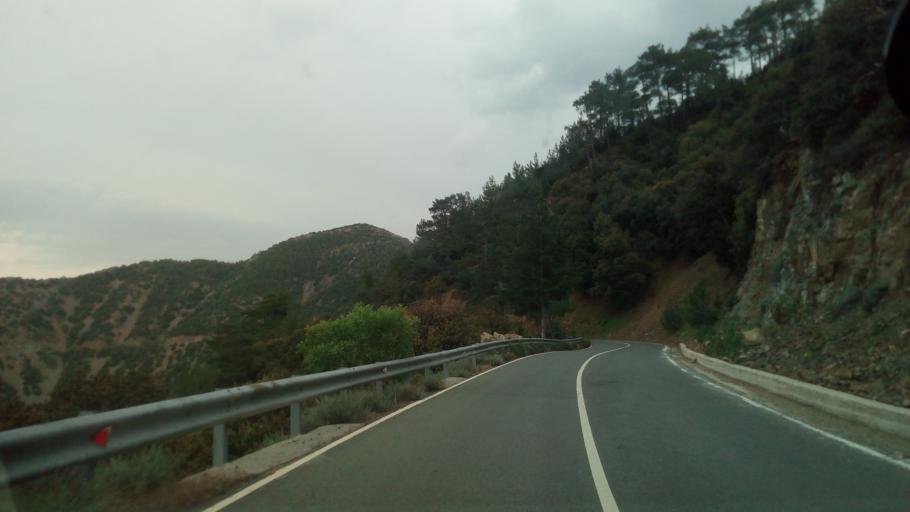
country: CY
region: Lefkosia
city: Kato Pyrgos
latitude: 34.9979
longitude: 32.6951
